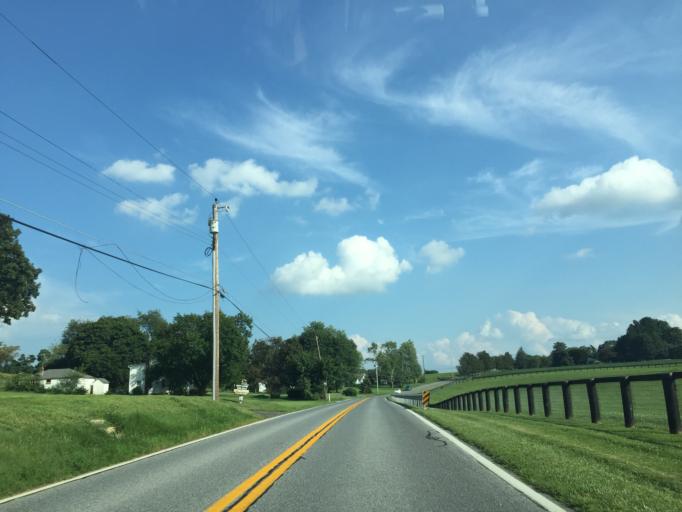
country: US
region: Maryland
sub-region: Carroll County
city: Hampstead
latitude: 39.6072
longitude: -76.7774
